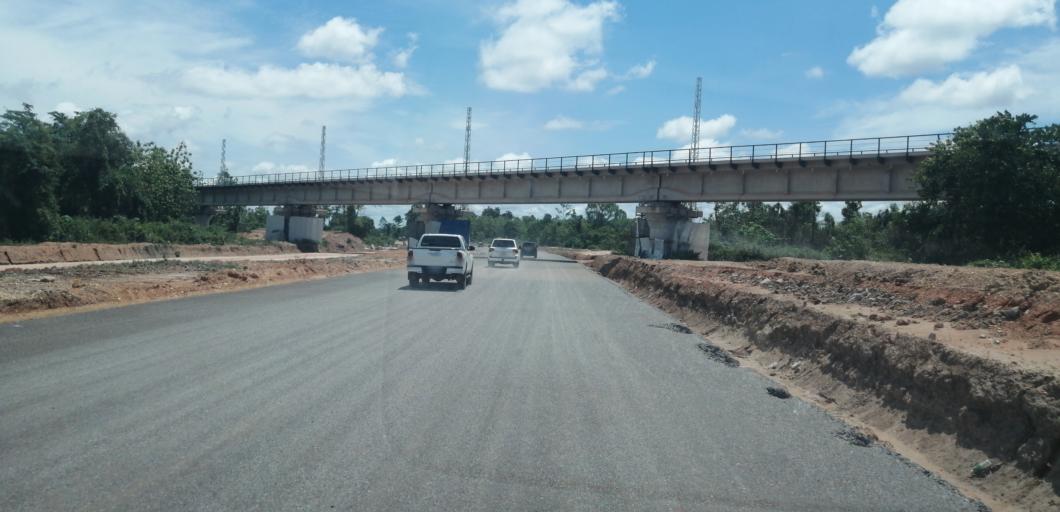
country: TH
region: Nong Khai
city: Sangkhom
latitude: 18.2263
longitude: 102.4817
